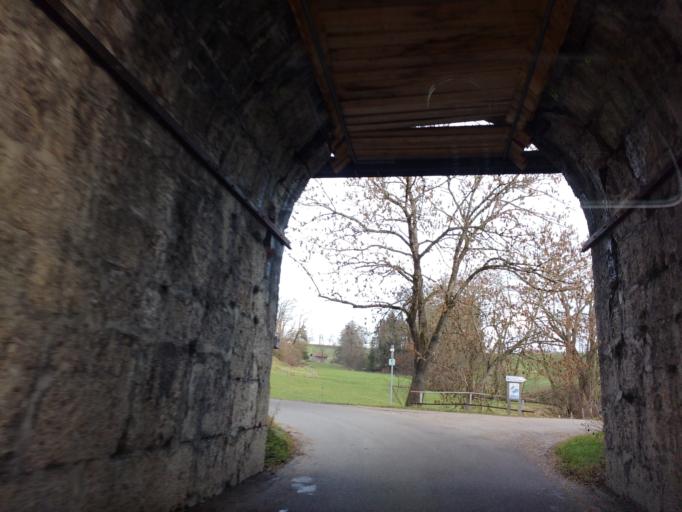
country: DE
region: Bavaria
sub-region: Swabia
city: Wildpoldsried
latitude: 47.7792
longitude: 10.4019
